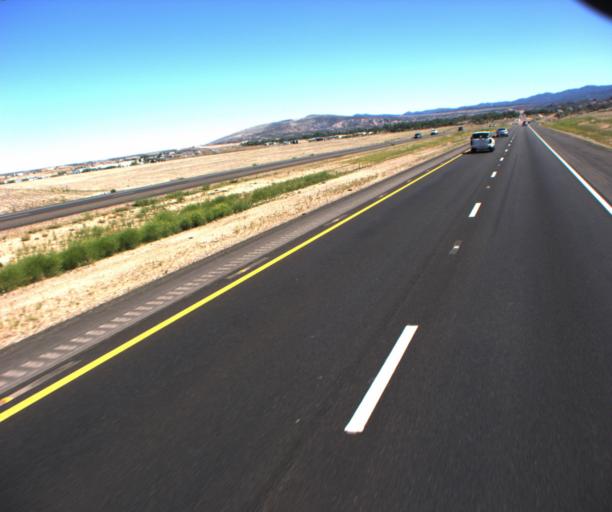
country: US
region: Arizona
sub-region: Yavapai County
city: Chino Valley
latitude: 34.6625
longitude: -112.4379
